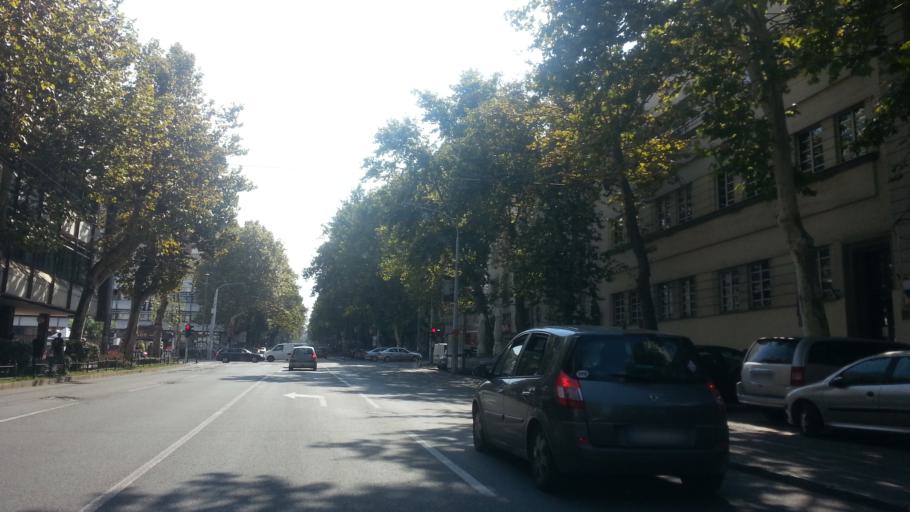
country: RS
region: Central Serbia
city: Belgrade
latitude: 44.8103
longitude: 20.4748
